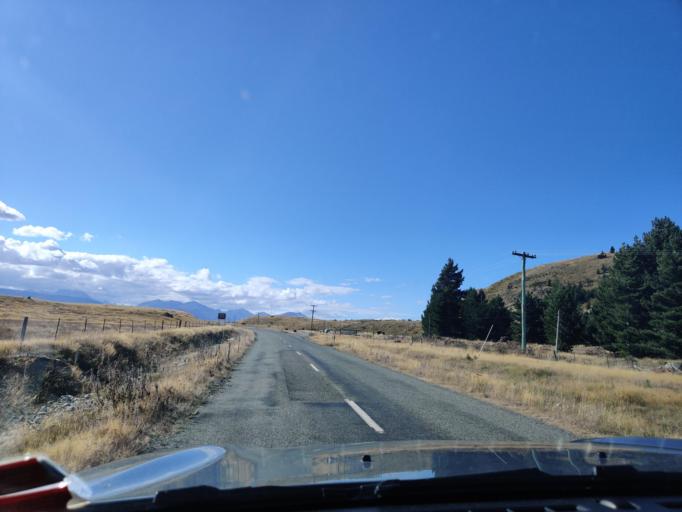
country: NZ
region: Canterbury
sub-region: Timaru District
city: Pleasant Point
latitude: -43.9961
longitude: 170.4514
